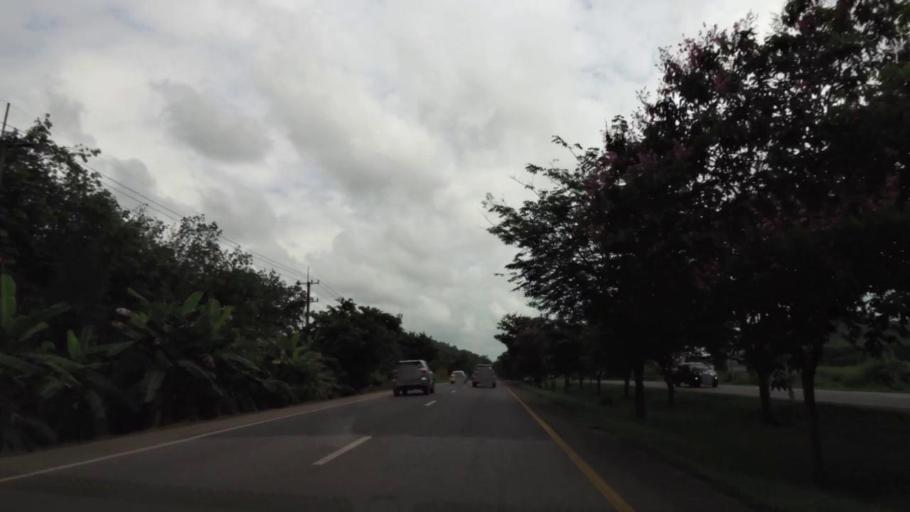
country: TH
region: Chanthaburi
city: Na Yai Am
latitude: 12.7368
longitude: 101.8965
